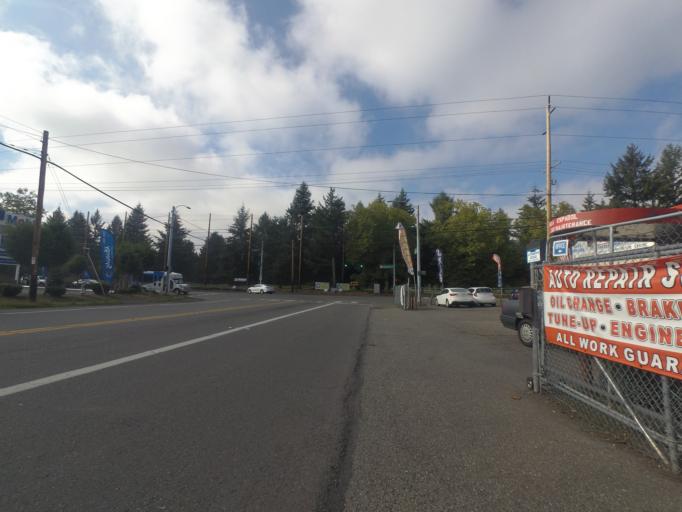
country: US
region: Washington
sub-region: Pierce County
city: Lakewood
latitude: 47.1975
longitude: -122.5081
